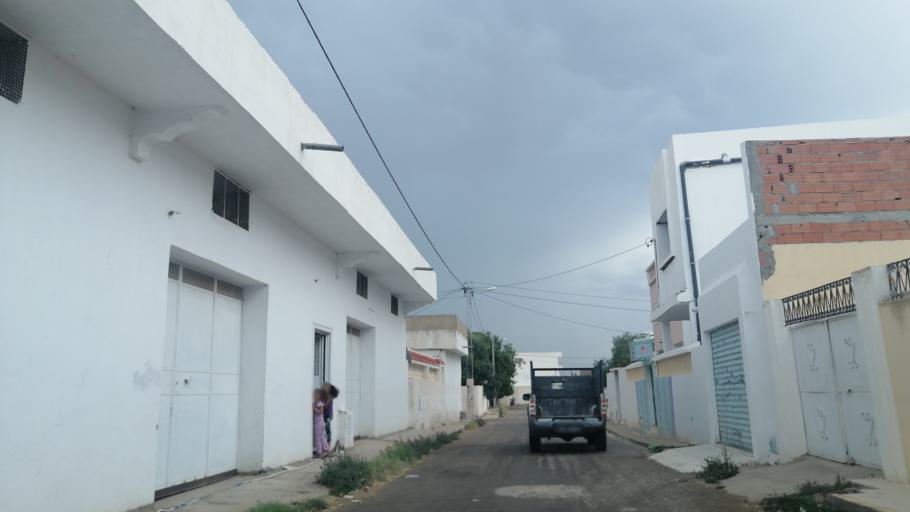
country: TN
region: Al Qayrawan
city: Sbikha
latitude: 36.1229
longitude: 10.0926
